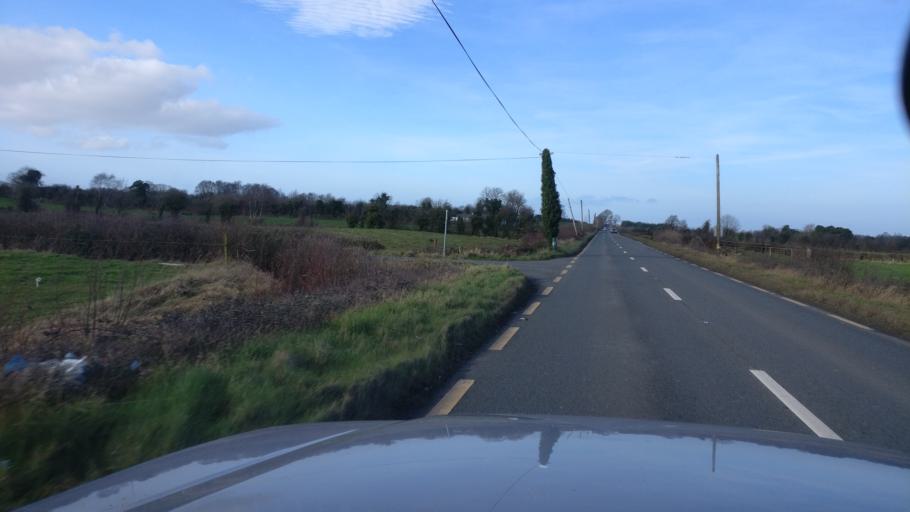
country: IE
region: Leinster
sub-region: Laois
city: Mountmellick
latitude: 53.0915
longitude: -7.3355
